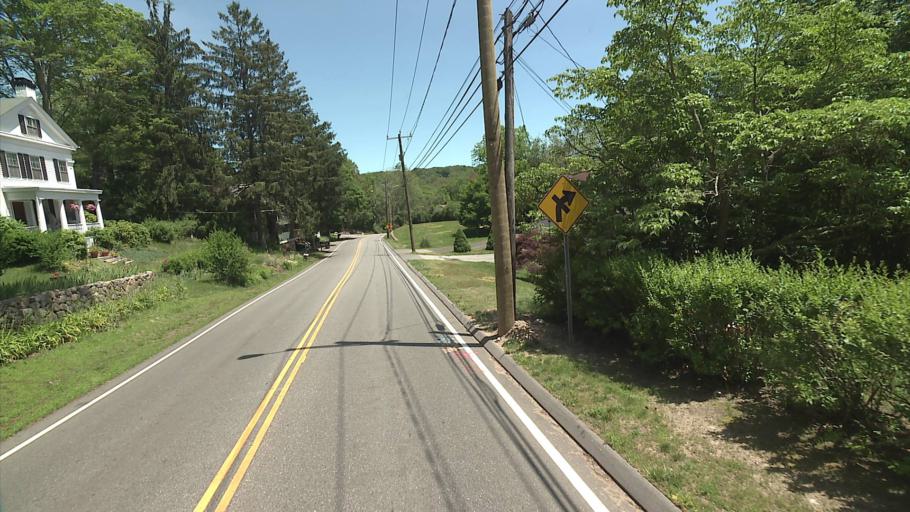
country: US
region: Connecticut
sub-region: New London County
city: Old Mystic
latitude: 41.3914
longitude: -71.9637
